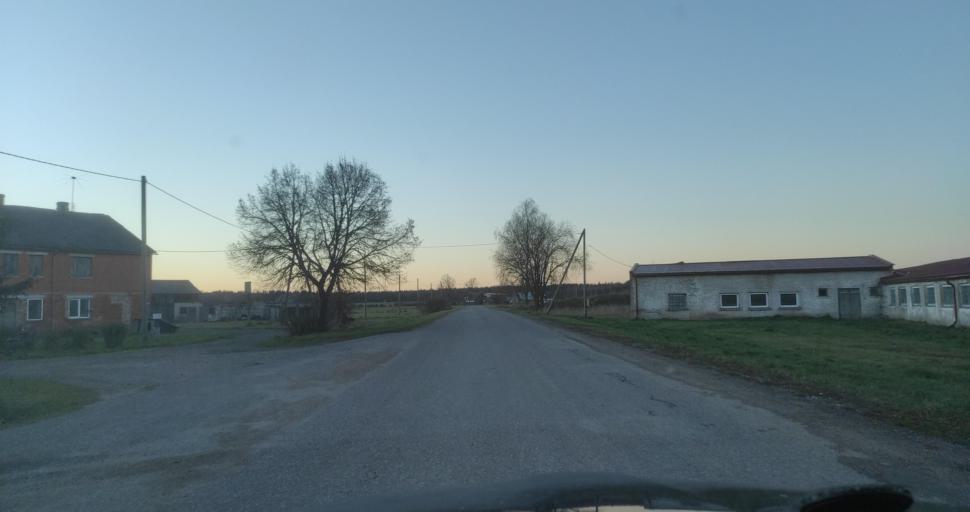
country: LV
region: Dundaga
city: Dundaga
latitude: 57.3758
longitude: 22.2286
